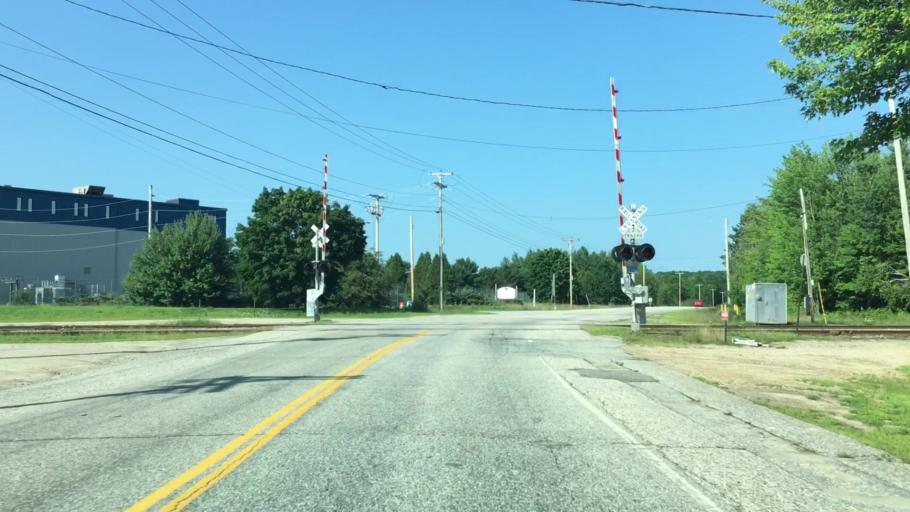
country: US
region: Maine
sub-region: Androscoggin County
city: Minot
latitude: 44.0464
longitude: -70.2984
